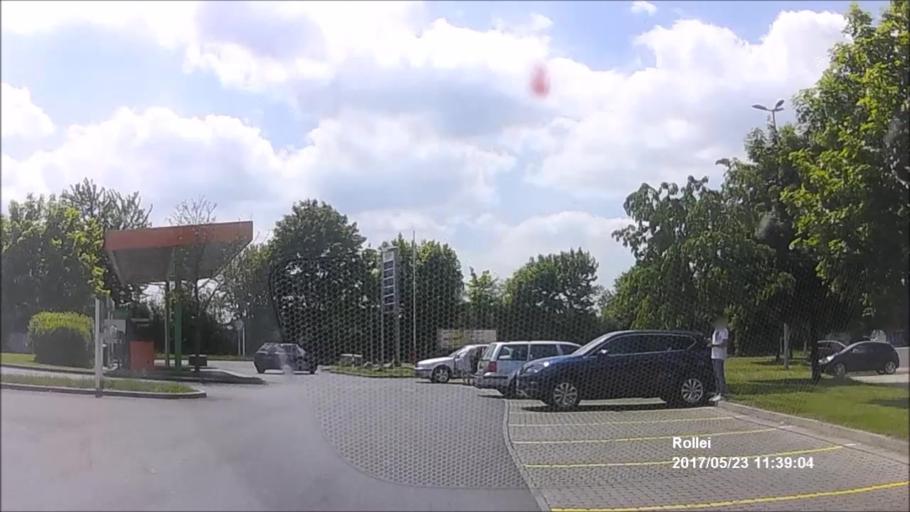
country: DE
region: Bavaria
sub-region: Upper Palatinate
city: Wackersdorf
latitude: 49.3129
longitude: 12.1471
